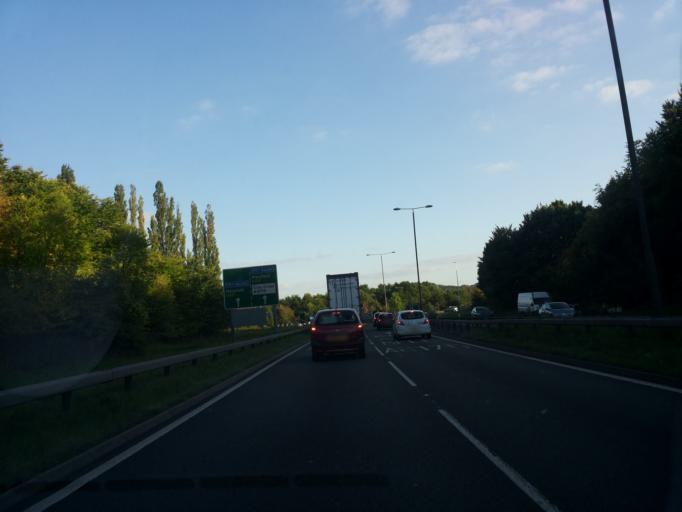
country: GB
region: England
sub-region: Derbyshire
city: Bolsover
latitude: 53.1993
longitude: -1.3269
